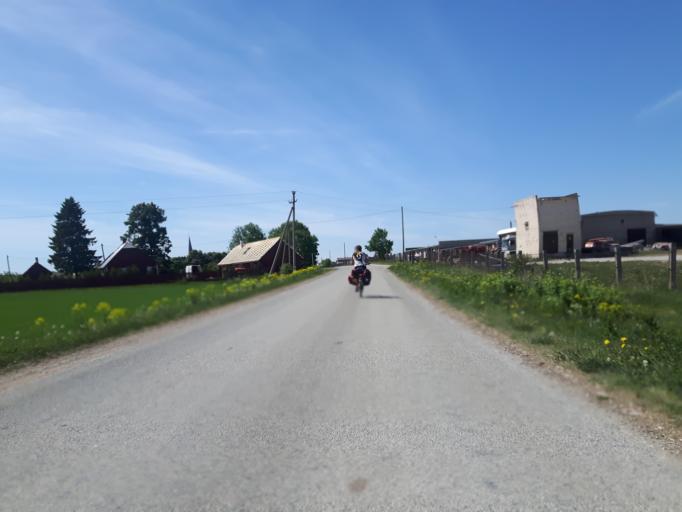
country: EE
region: Laeaene-Virumaa
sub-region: Viru-Nigula vald
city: Kunda
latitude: 59.4511
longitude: 26.6954
